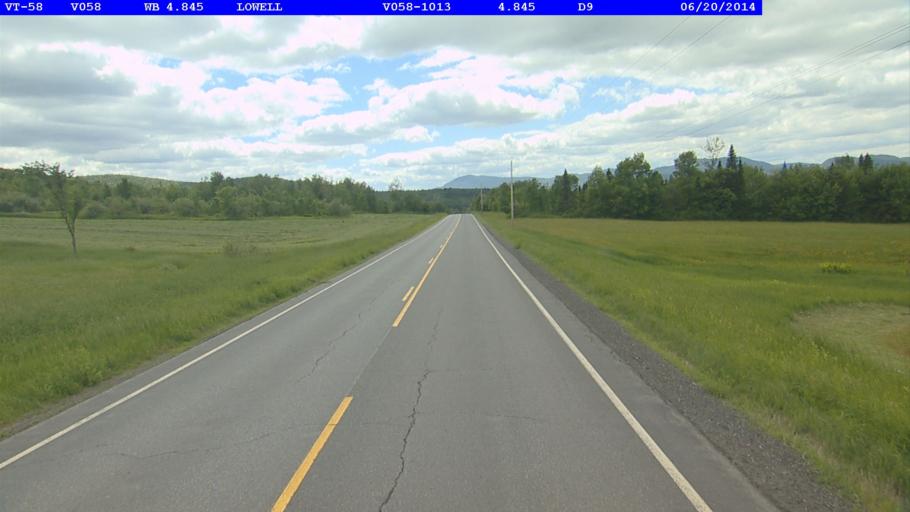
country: US
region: Vermont
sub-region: Orleans County
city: Newport
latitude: 44.8185
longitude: -72.3642
